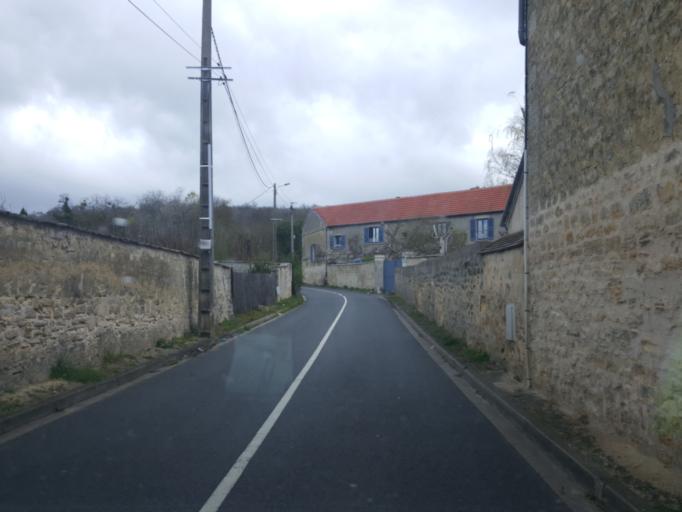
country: FR
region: Ile-de-France
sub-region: Departement du Val-d'Oise
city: Magny-en-Vexin
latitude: 49.1641
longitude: 1.7807
